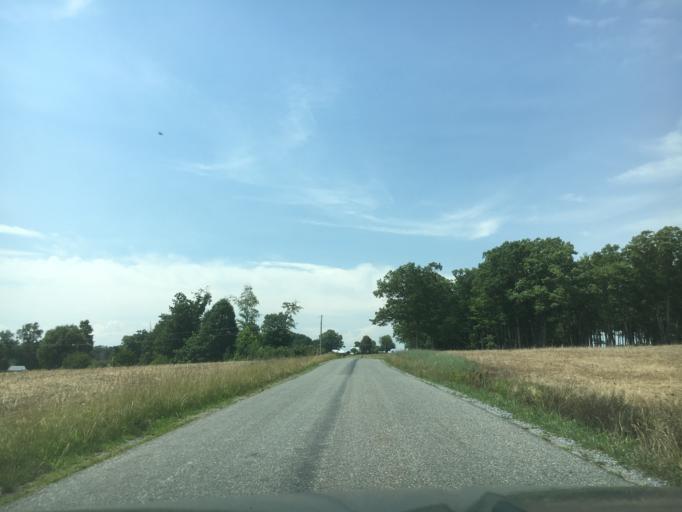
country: US
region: Virginia
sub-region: Pittsylvania County
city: Gretna
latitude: 36.9019
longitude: -79.4072
